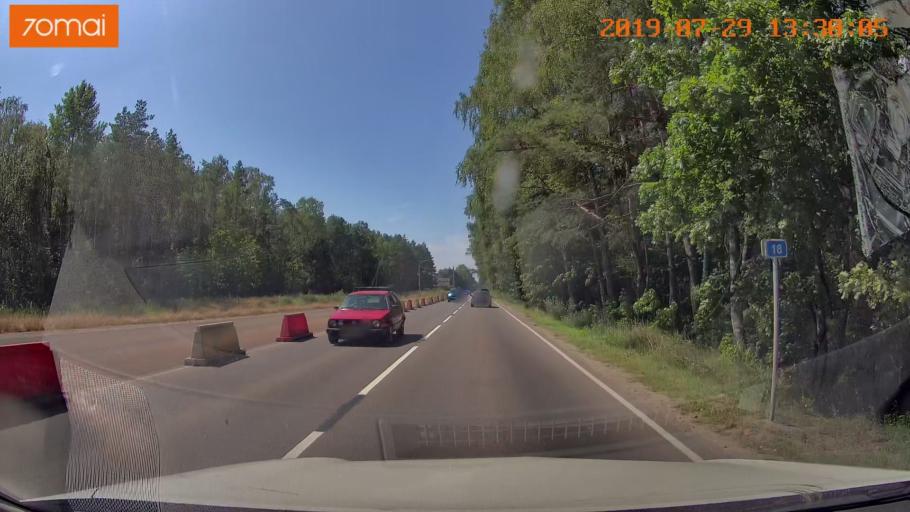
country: RU
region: Kaliningrad
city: Vzmorye
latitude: 54.7003
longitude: 20.2594
